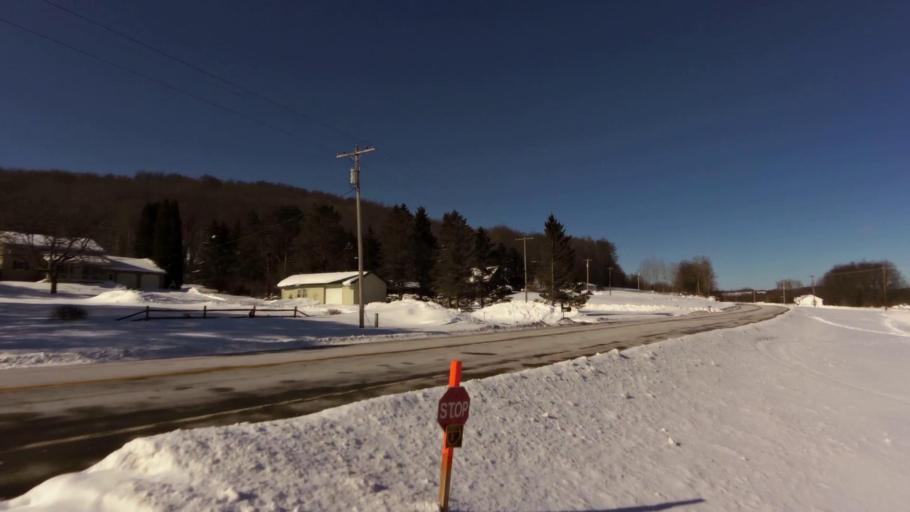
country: US
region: New York
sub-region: Cattaraugus County
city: Franklinville
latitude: 42.4044
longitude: -78.5023
